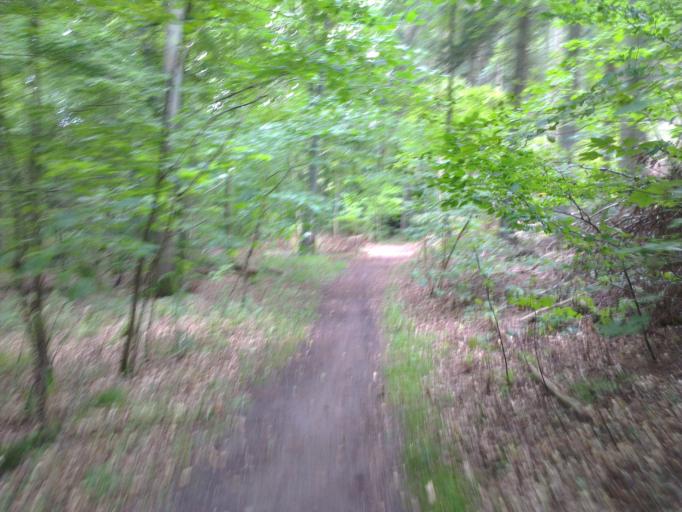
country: DK
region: Capital Region
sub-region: Frederikssund Kommune
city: Frederikssund
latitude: 55.8466
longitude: 12.0274
